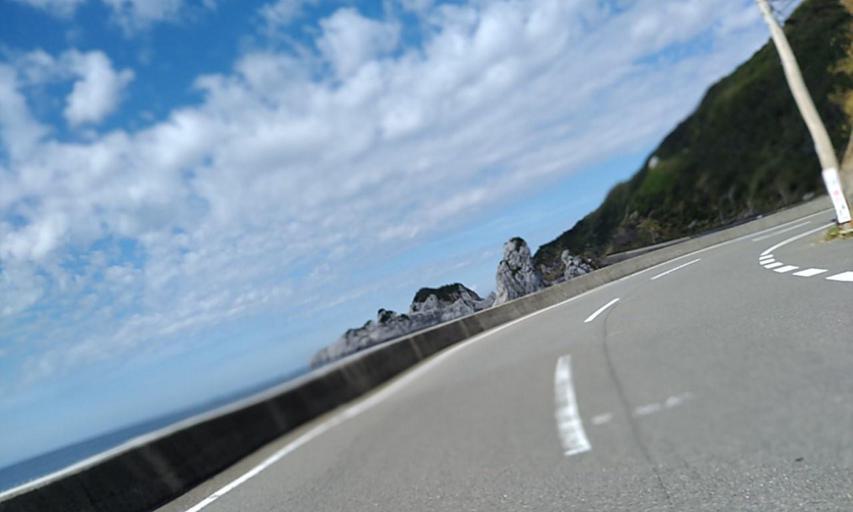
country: JP
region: Wakayama
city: Gobo
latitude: 33.9700
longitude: 135.0792
